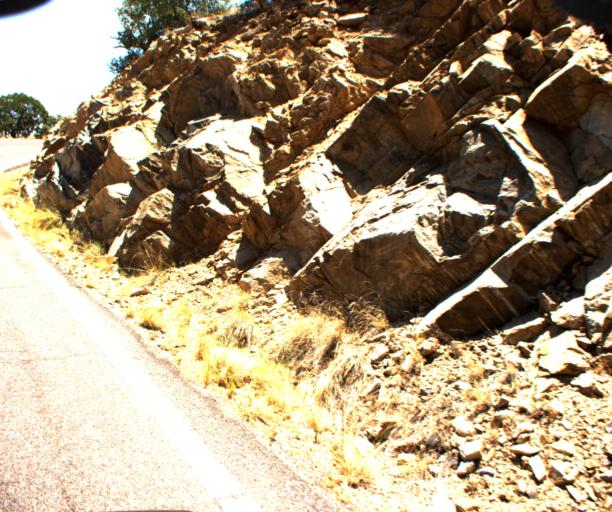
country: US
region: Arizona
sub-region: Graham County
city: Swift Trail Junction
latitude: 32.6664
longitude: -109.8024
